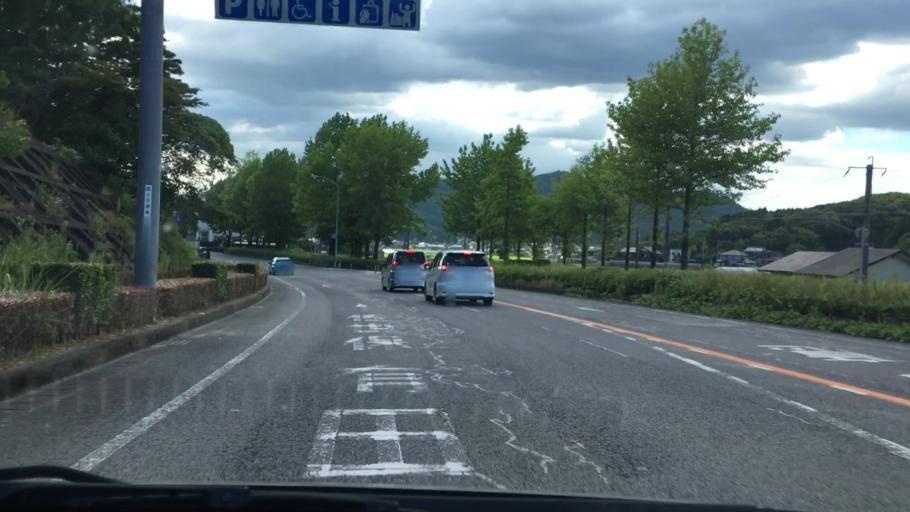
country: JP
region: Saga Prefecture
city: Takeocho-takeo
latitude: 33.1968
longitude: 129.9739
